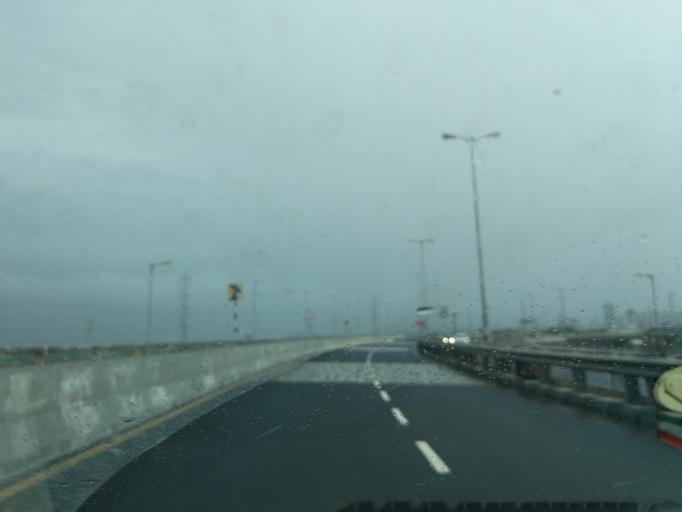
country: IN
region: Maharashtra
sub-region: Mumbai Suburban
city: Mumbai
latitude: 19.0130
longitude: 72.8714
